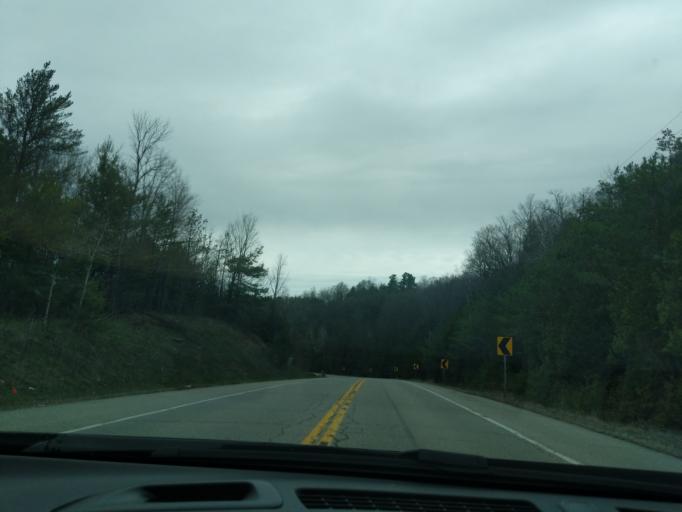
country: CA
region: Ontario
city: Orangeville
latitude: 43.9978
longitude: -80.0031
